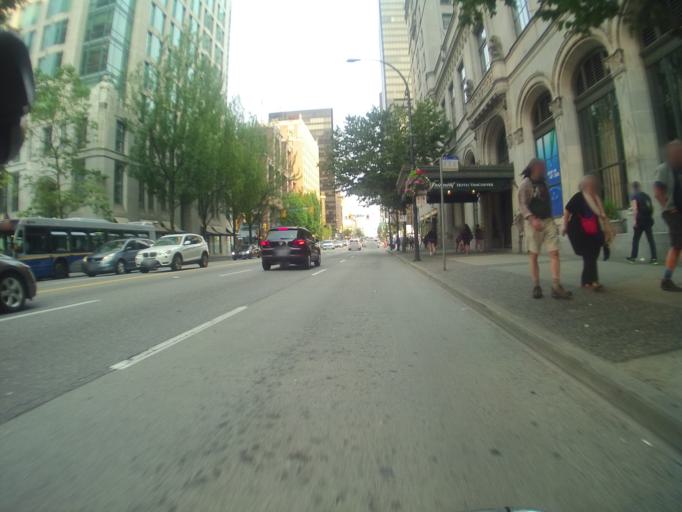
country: CA
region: British Columbia
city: West End
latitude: 49.2843
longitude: -123.1210
